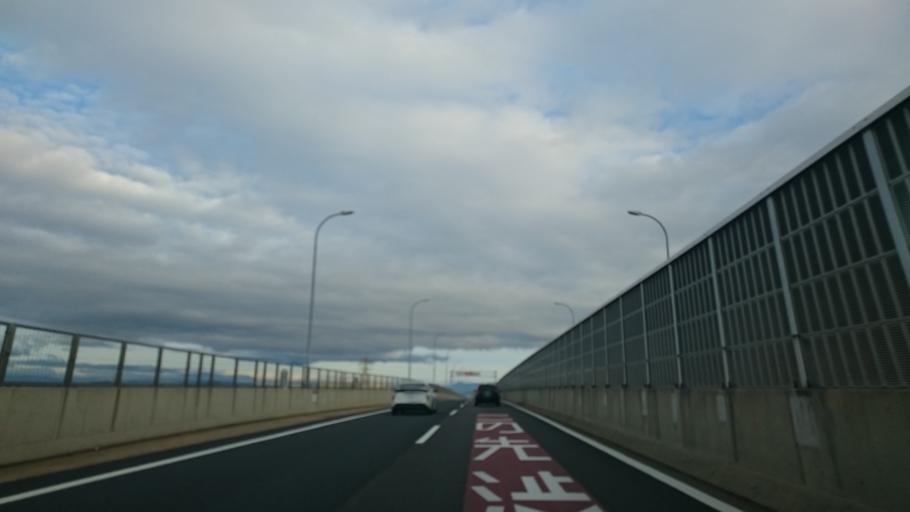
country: JP
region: Aichi
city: Komaki
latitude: 35.2782
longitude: 136.9066
